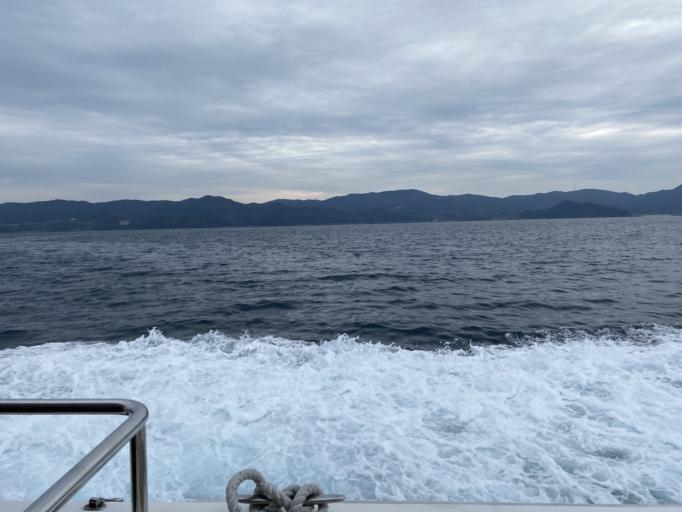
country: JP
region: Nagasaki
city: Nagasaki-shi
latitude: 32.6377
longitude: 129.7601
